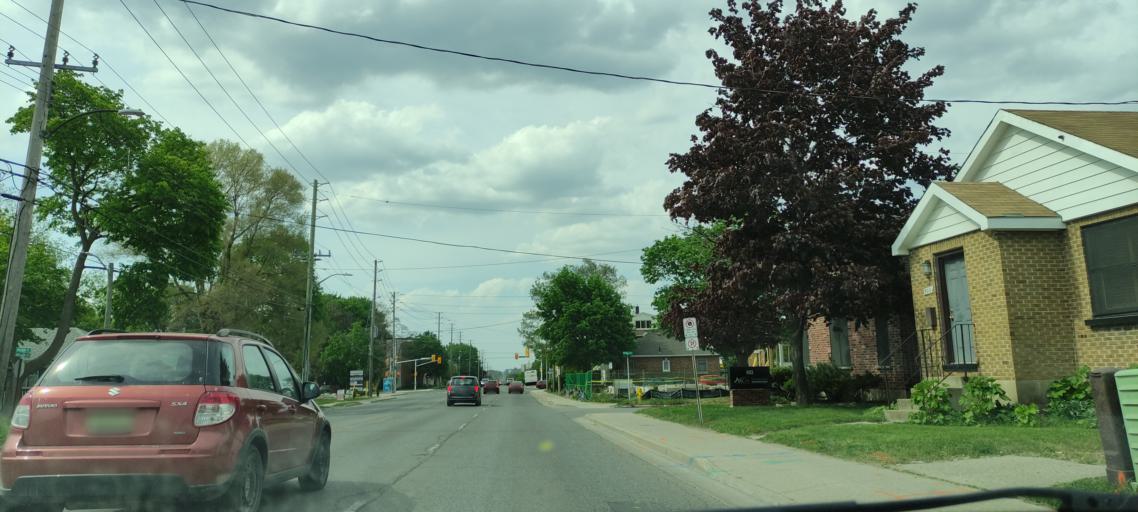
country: CA
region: Ontario
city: London
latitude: 43.0048
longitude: -81.2394
